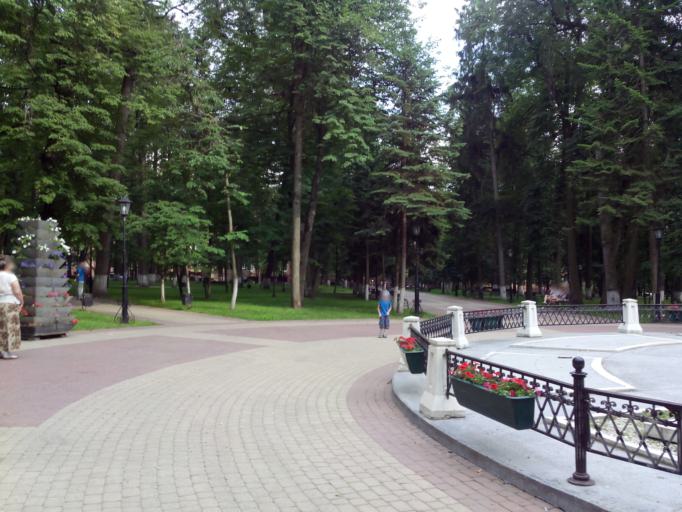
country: RU
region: Kaluga
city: Kaluga
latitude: 54.5154
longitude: 36.2320
